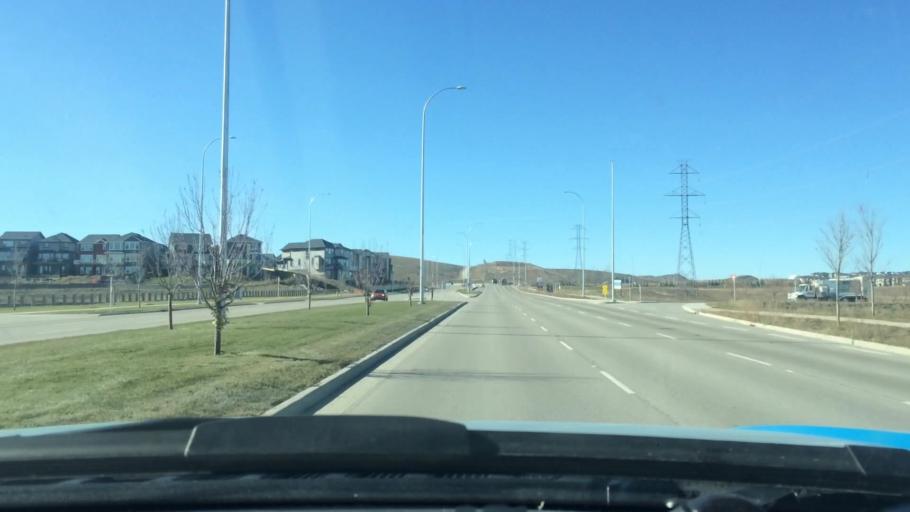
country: CA
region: Alberta
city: Calgary
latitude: 51.1681
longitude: -114.1549
